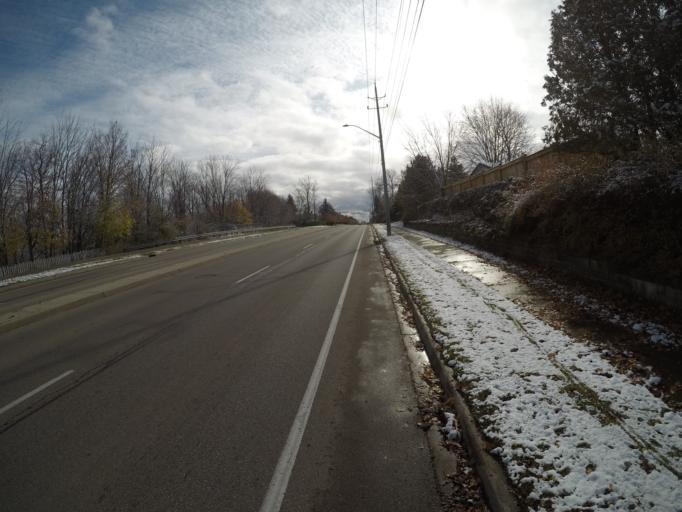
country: CA
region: Ontario
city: Waterloo
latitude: 43.5029
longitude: -80.4956
